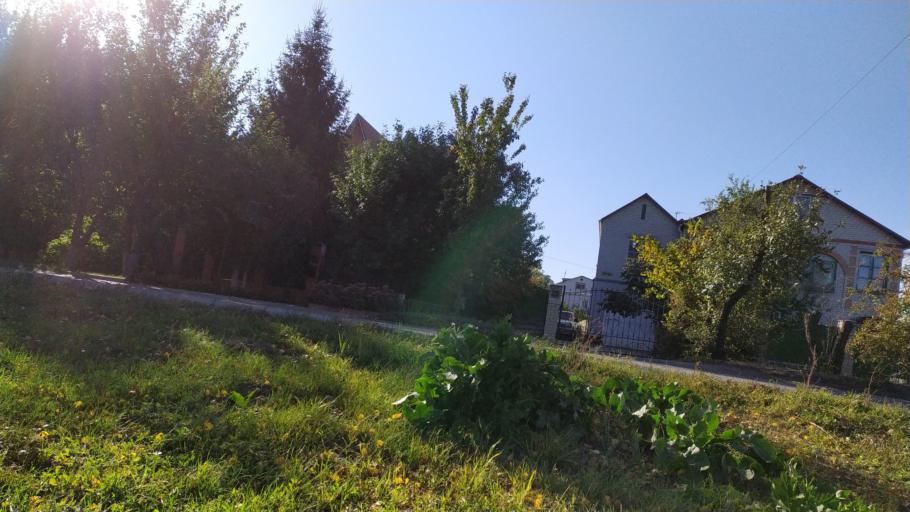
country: RU
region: Kursk
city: Kursk
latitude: 51.6437
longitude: 36.1395
